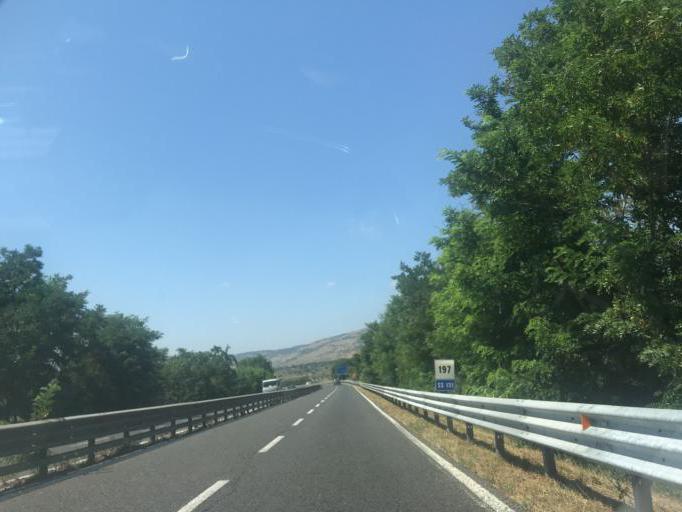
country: IT
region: Sardinia
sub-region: Provincia di Sassari
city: Codrongianos
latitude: 40.6645
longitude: 8.6682
